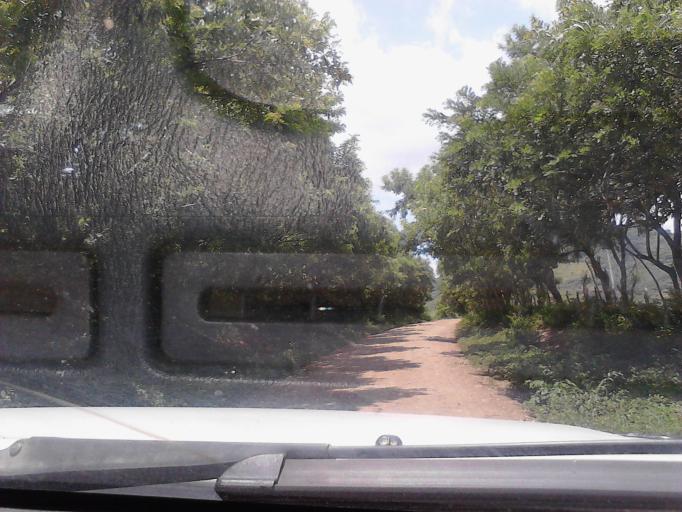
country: NI
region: Matagalpa
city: Terrabona
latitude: 12.6918
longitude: -85.9538
